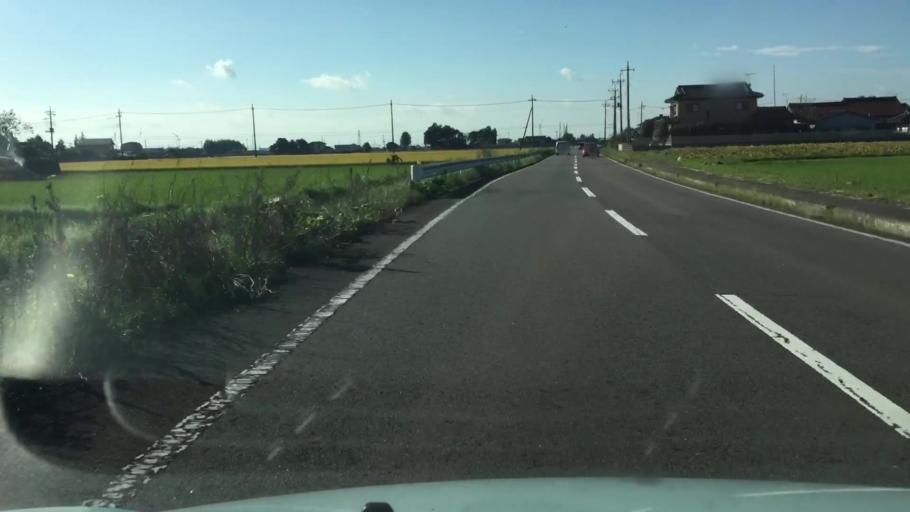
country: JP
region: Tochigi
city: Ujiie
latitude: 36.6673
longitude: 140.0187
